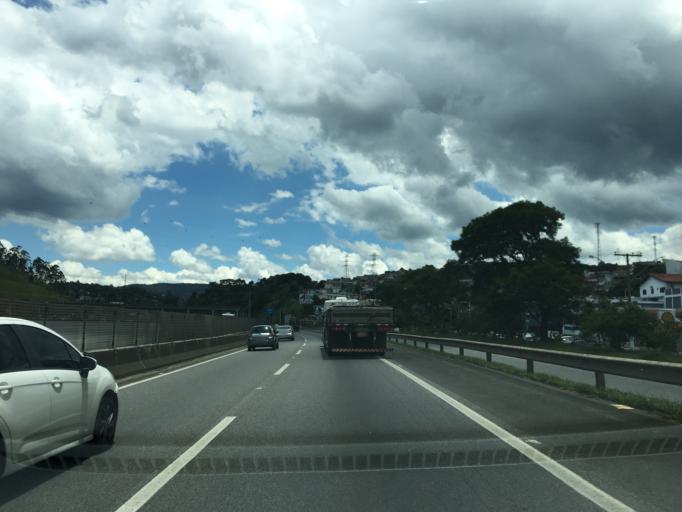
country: BR
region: Sao Paulo
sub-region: Mairipora
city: Mairipora
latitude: -23.3203
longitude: -46.5824
